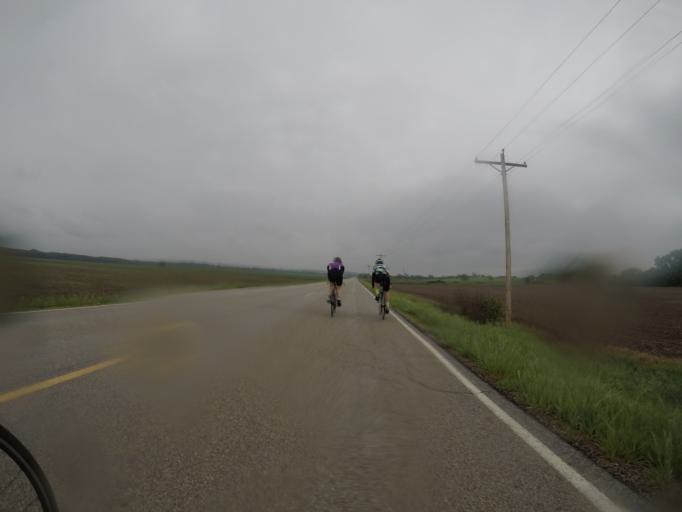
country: US
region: Kansas
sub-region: Pottawatomie County
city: Wamego
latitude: 39.3201
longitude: -96.2215
